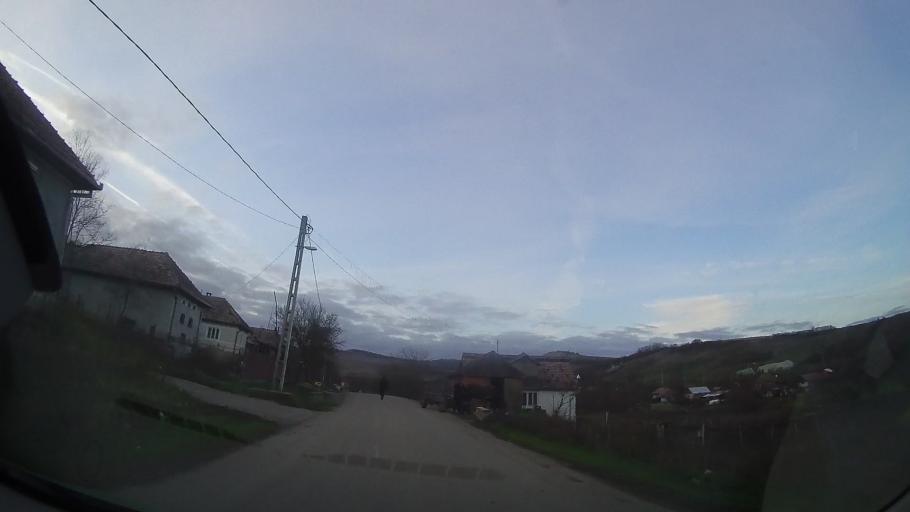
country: RO
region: Cluj
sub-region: Comuna Geaca
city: Geaca
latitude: 46.8522
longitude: 24.0511
